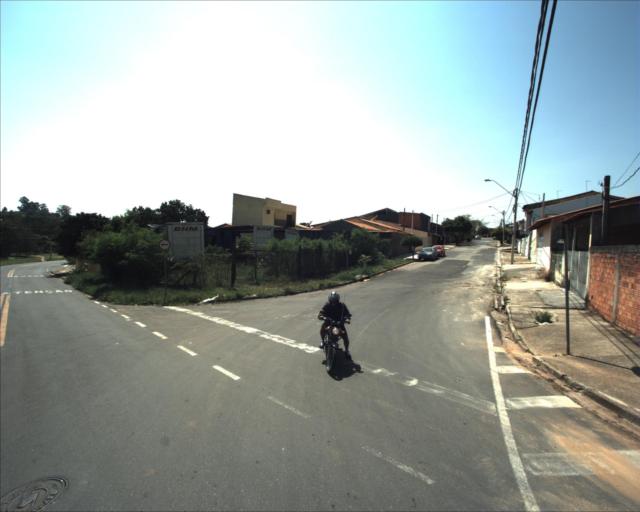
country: BR
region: Sao Paulo
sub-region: Sorocaba
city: Sorocaba
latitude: -23.4598
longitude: -47.4965
